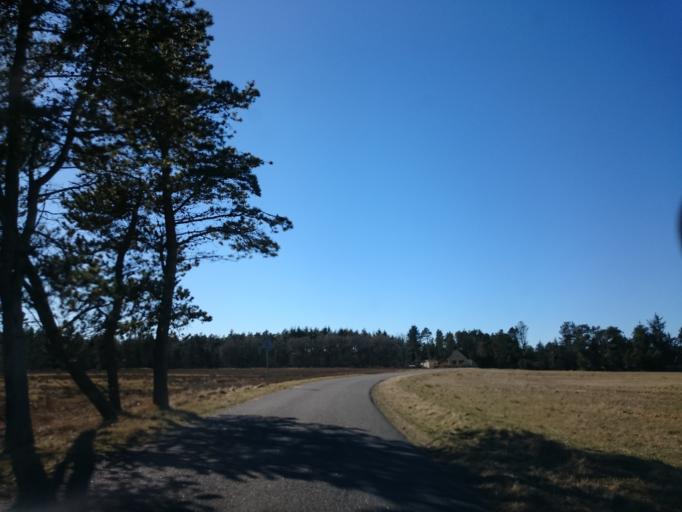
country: DK
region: North Denmark
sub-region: Hjorring Kommune
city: Sindal
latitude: 57.6200
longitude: 10.3120
